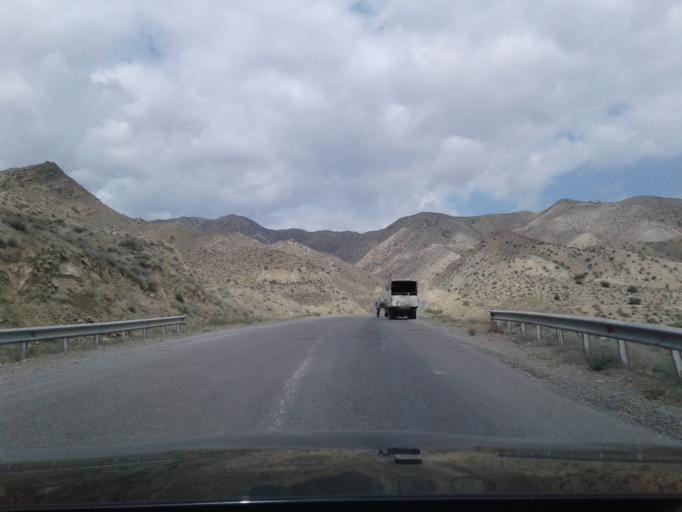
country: TM
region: Ahal
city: Baharly
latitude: 38.5042
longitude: 57.0650
